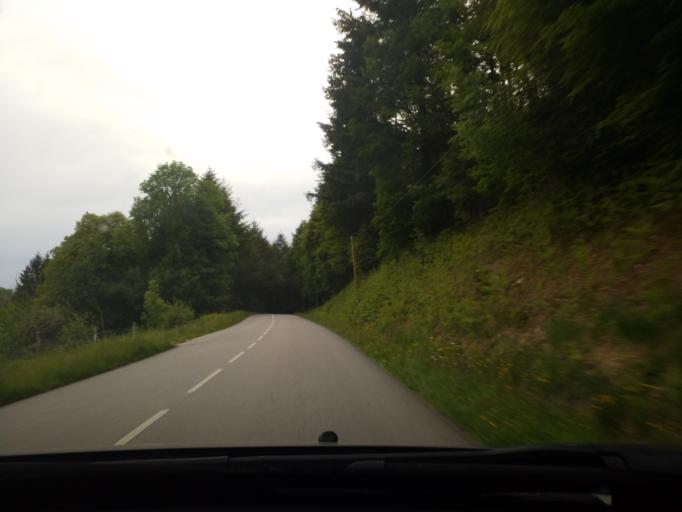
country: FR
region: Lorraine
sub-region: Departement des Vosges
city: Bains-les-Bains
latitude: 48.0309
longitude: 6.1965
